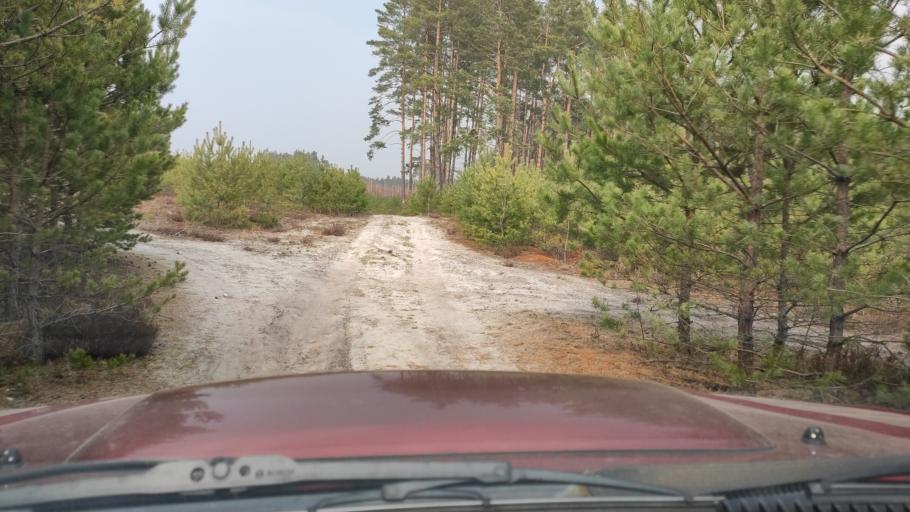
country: PL
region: Masovian Voivodeship
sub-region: Powiat zwolenski
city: Zwolen
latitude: 51.3904
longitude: 21.5713
